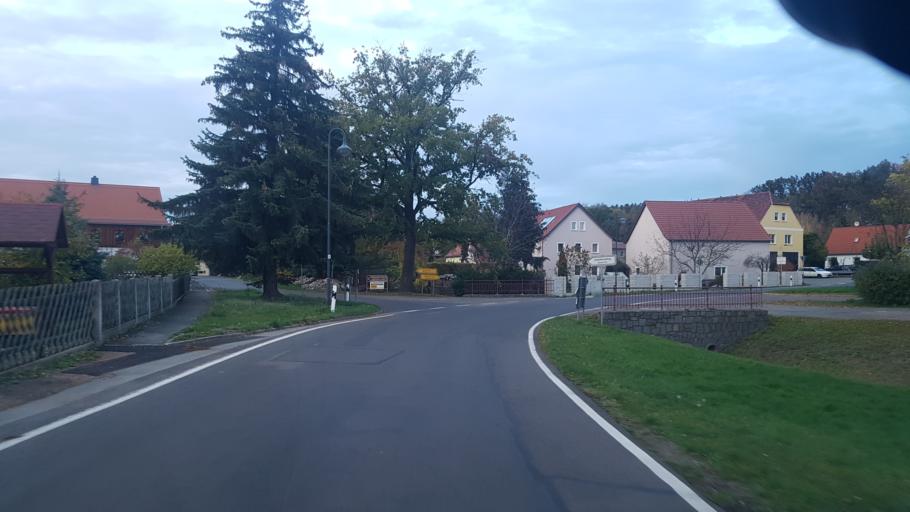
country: DE
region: Saxony
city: Cavertitz
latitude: 51.3902
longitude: 13.0951
